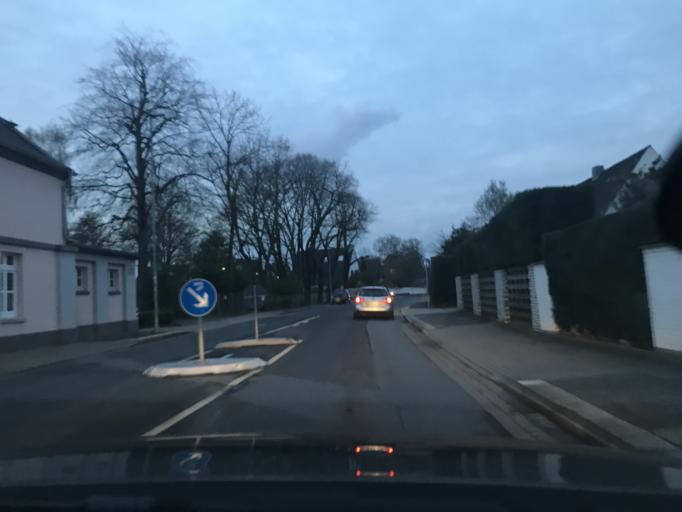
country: DE
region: North Rhine-Westphalia
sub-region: Regierungsbezirk Dusseldorf
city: Moers
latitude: 51.4414
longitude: 6.6222
